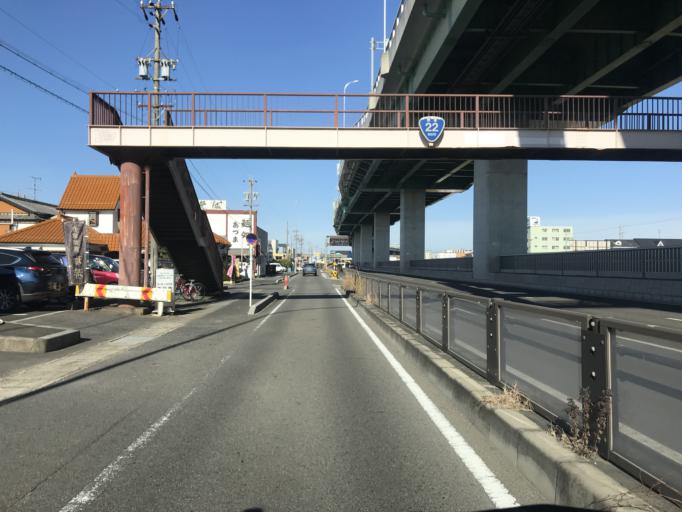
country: JP
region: Aichi
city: Nagoya-shi
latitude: 35.2125
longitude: 136.8608
